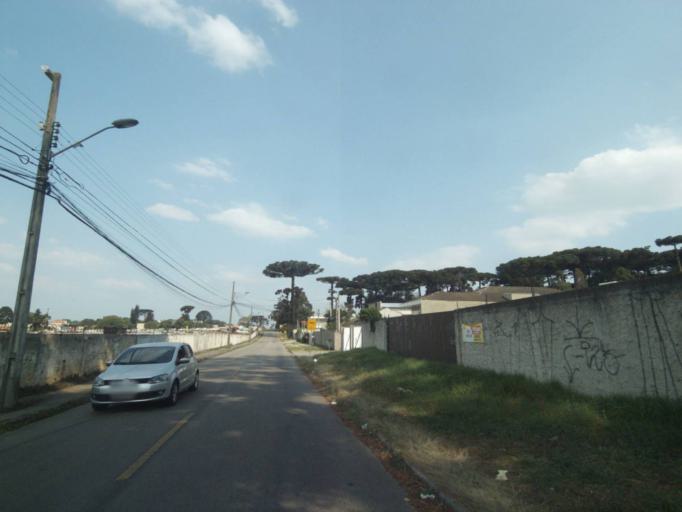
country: BR
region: Parana
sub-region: Sao Jose Dos Pinhais
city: Sao Jose dos Pinhais
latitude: -25.5112
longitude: -49.2502
